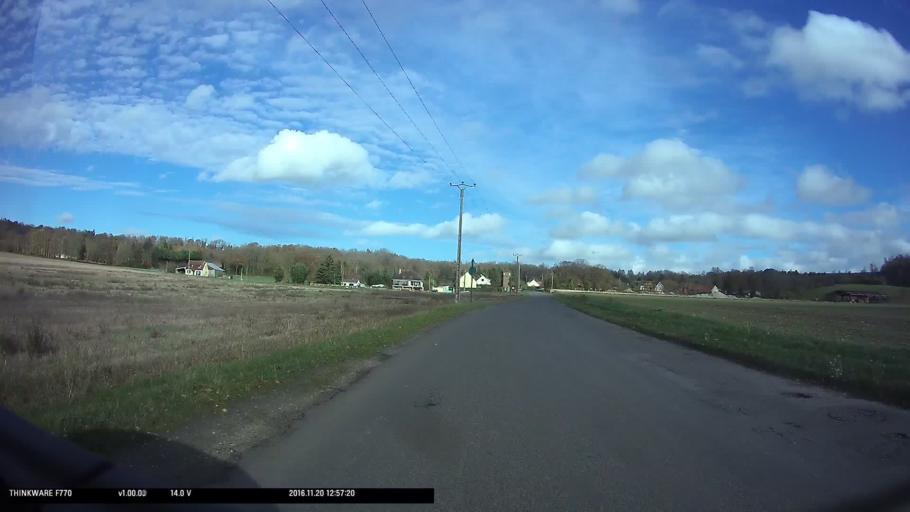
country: FR
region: Ile-de-France
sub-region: Departement du Val-d'Oise
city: Sagy
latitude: 49.0535
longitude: 1.9533
